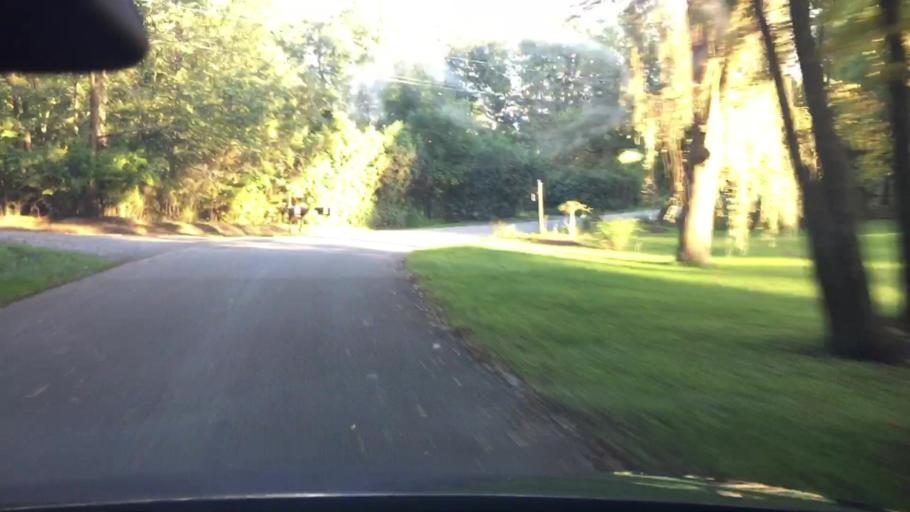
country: US
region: Pennsylvania
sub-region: Butler County
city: Nixon
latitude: 40.7694
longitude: -79.8864
